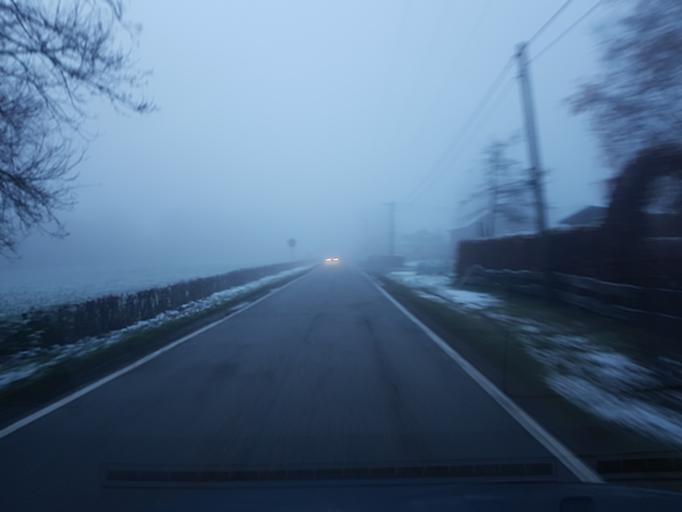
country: BE
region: Wallonia
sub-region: Province de Liege
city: Theux
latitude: 50.4926
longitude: 5.7688
